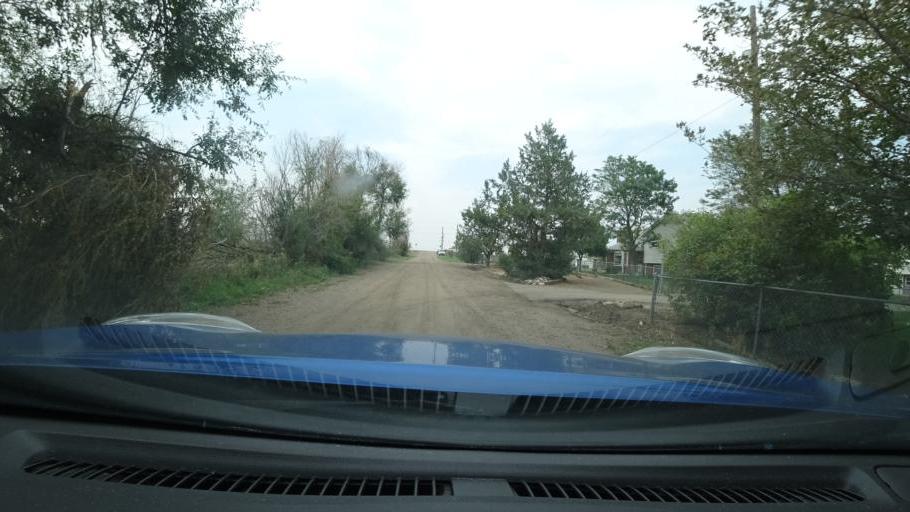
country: US
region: Colorado
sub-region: Adams County
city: Aurora
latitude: 39.7513
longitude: -104.7638
